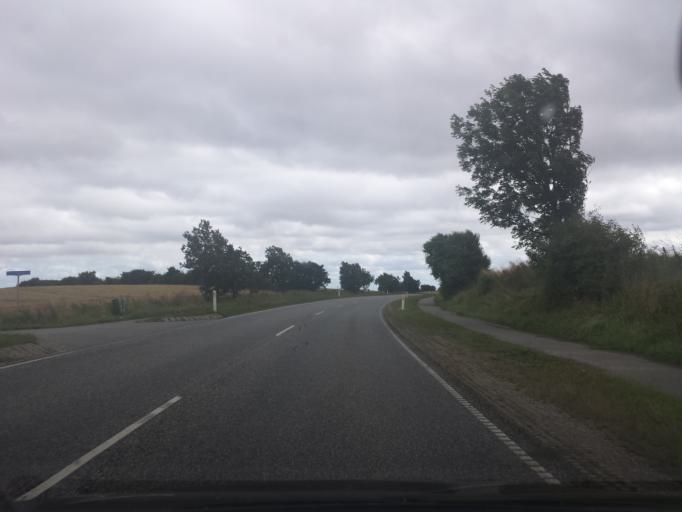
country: DK
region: South Denmark
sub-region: Sonderborg Kommune
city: Guderup
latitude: 55.0168
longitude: 9.8458
